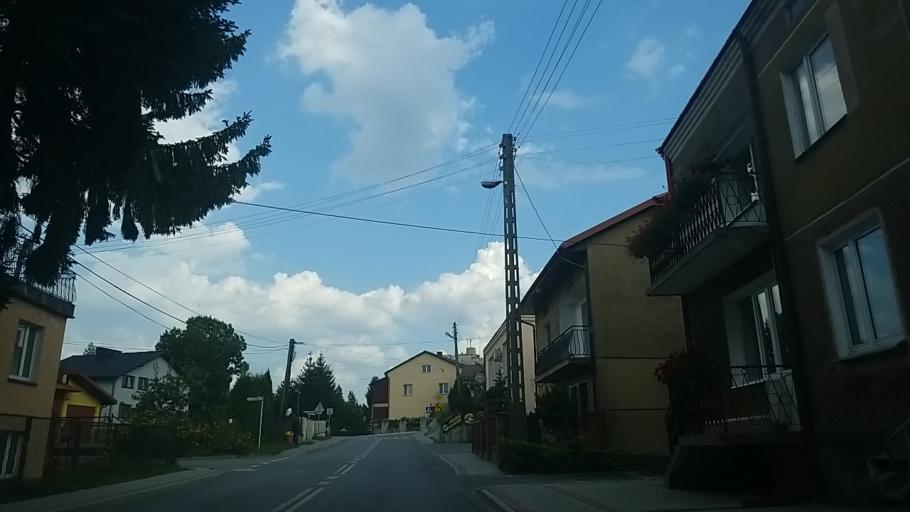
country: PL
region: Lublin Voivodeship
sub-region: Powiat bilgorajski
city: Goraj
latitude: 50.7217
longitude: 22.6646
